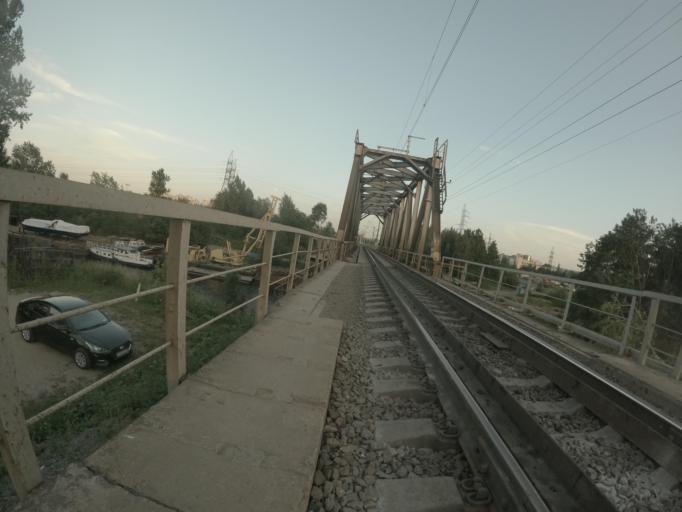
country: RU
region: St.-Petersburg
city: Krasnogvargeisky
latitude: 59.9416
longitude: 30.4479
